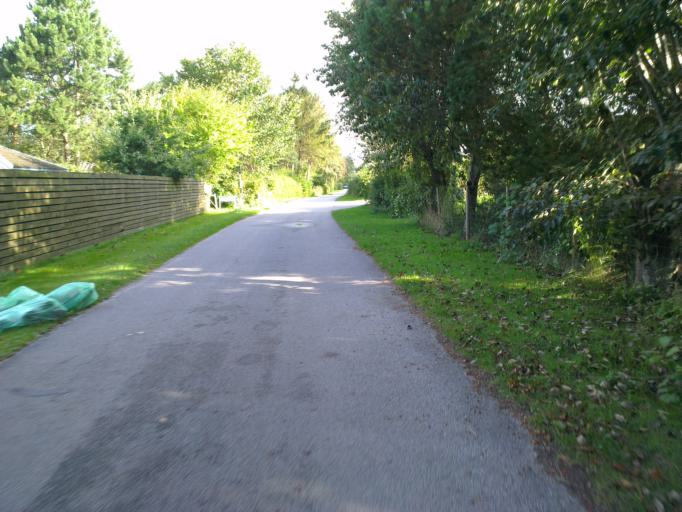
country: DK
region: Capital Region
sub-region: Frederikssund Kommune
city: Jaegerspris
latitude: 55.8314
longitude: 11.9529
